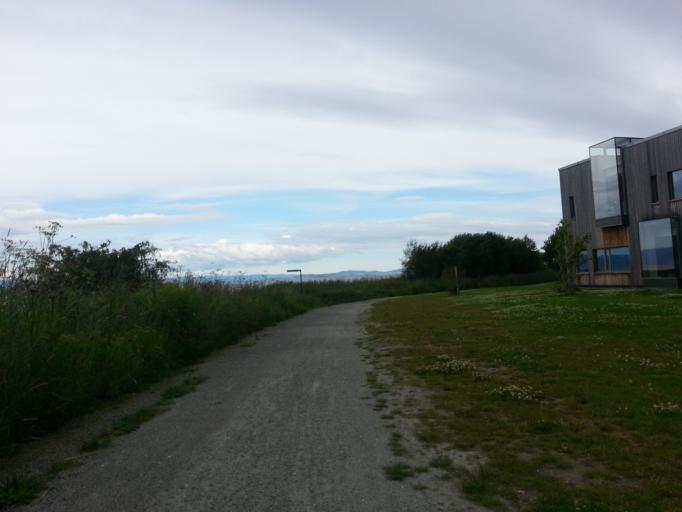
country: NO
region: Sor-Trondelag
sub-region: Trondheim
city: Trondheim
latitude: 63.4299
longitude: 10.5216
